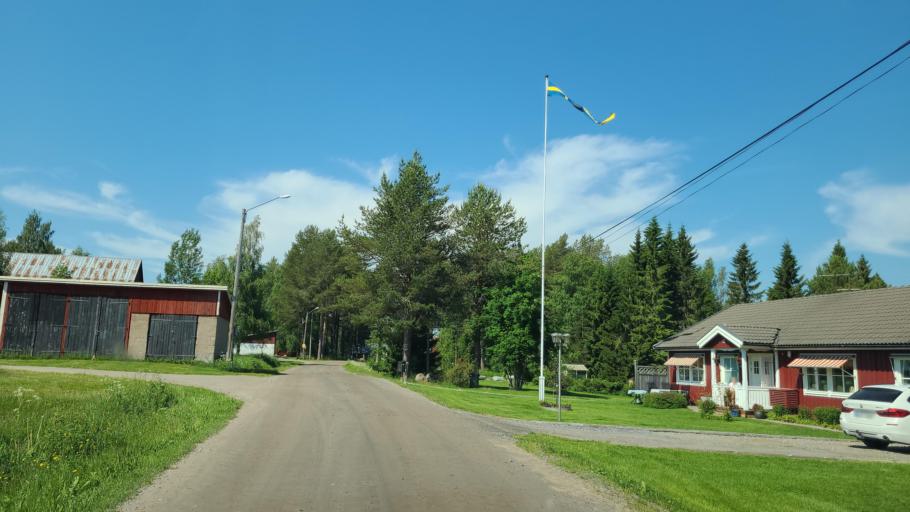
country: SE
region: Vaesterbotten
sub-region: Robertsfors Kommun
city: Robertsfors
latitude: 64.0795
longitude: 20.8595
